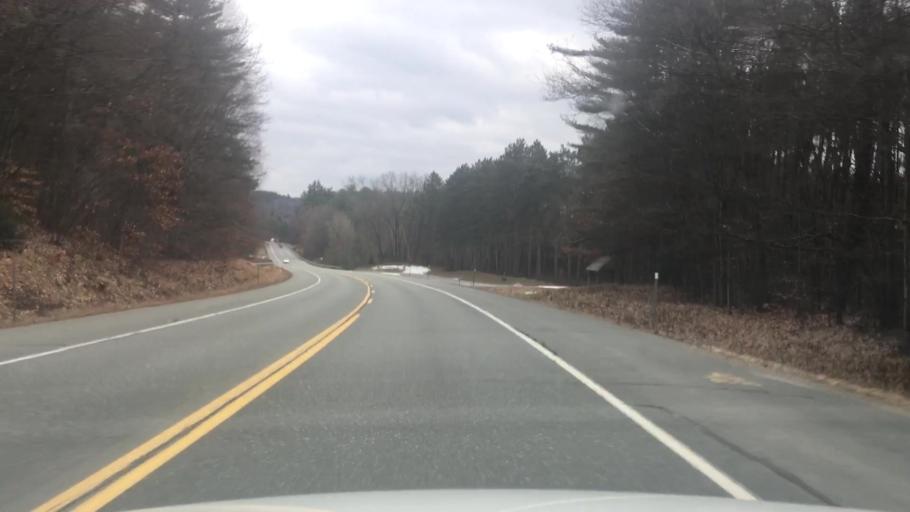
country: US
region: Vermont
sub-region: Windham County
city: Bellows Falls
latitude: 43.0532
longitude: -72.4473
